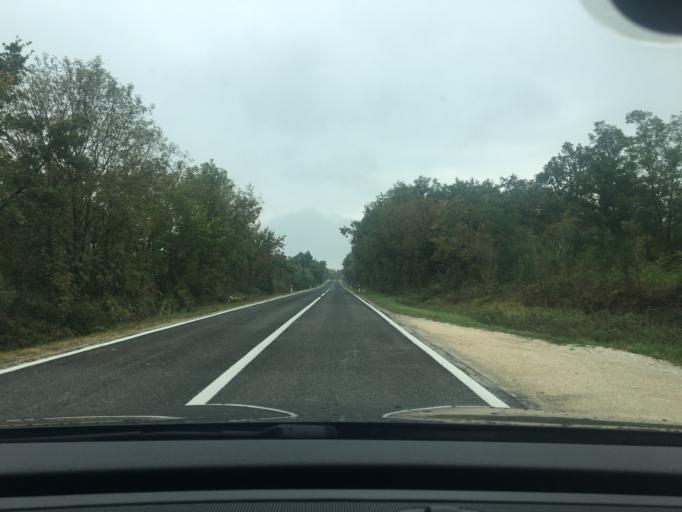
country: HR
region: Istarska
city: Buje
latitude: 45.4296
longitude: 13.6569
